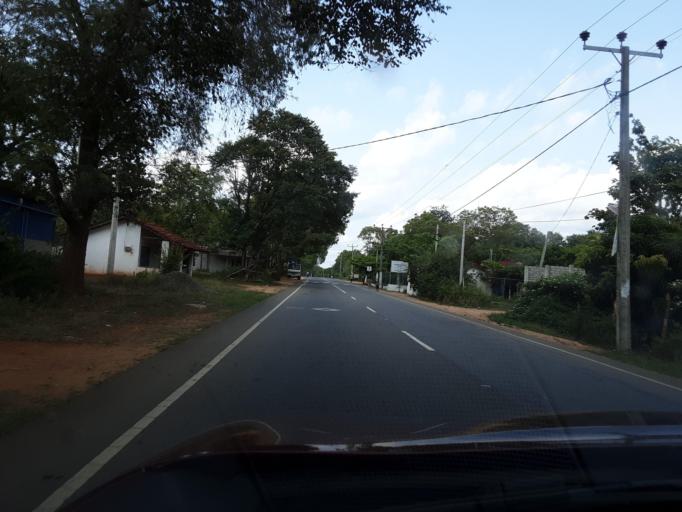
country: LK
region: Uva
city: Haputale
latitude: 6.5328
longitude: 81.1313
